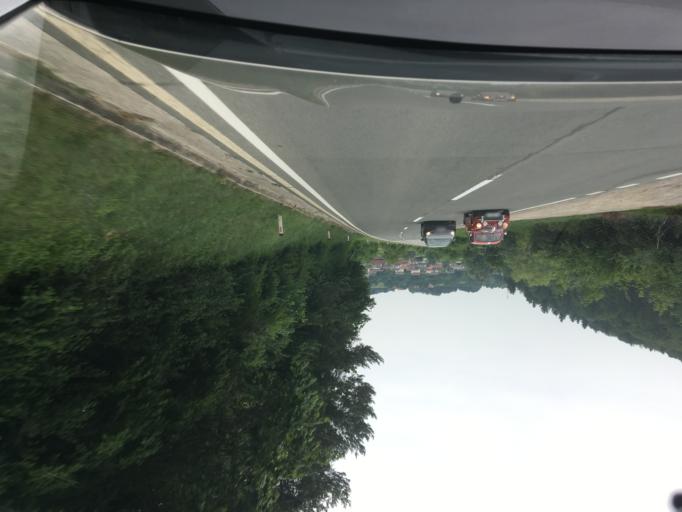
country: SI
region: Skofljica
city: Skofljica
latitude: 45.9821
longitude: 14.5907
